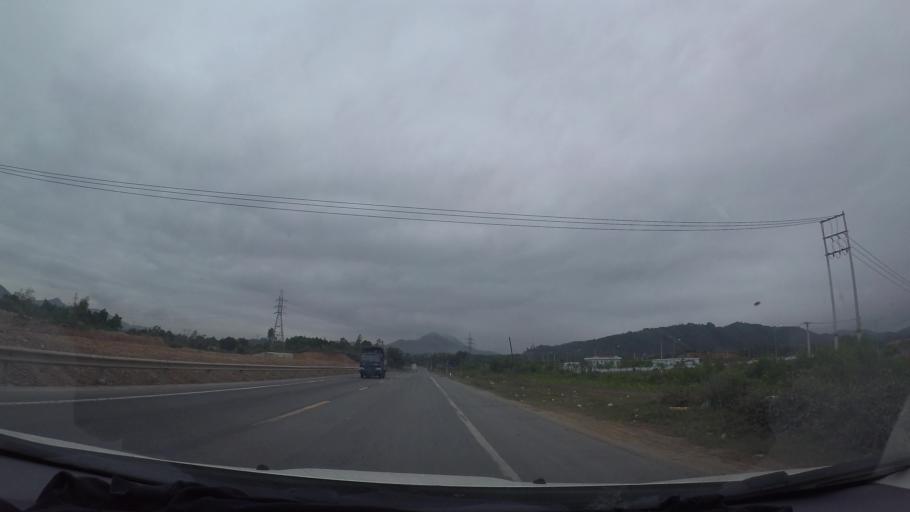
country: VN
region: Da Nang
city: Lien Chieu
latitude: 16.0848
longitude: 108.0847
